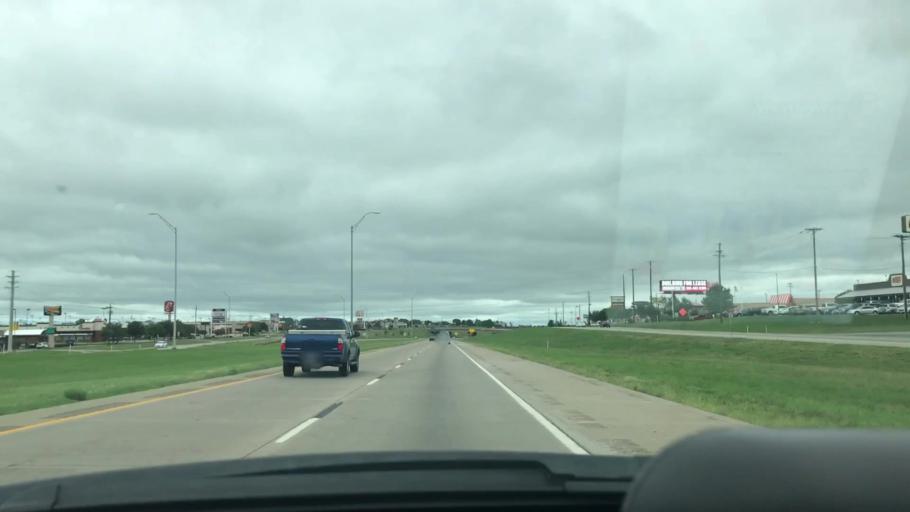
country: US
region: Texas
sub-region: Grayson County
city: Sherman
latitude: 33.6738
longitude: -96.6094
